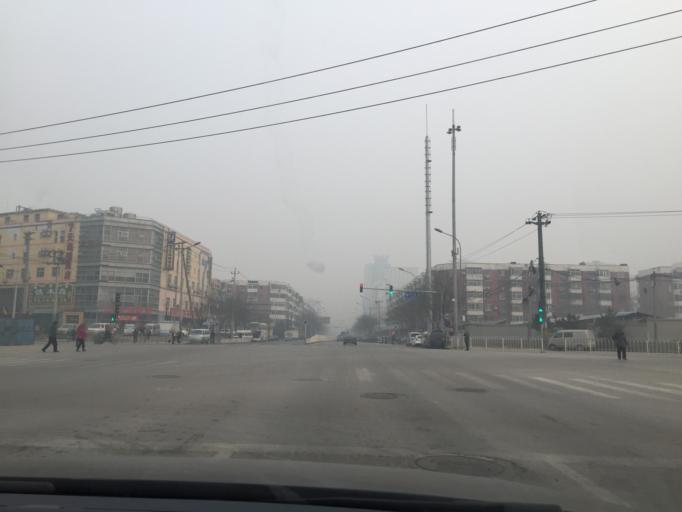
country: CN
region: Beijing
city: Qinghe
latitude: 40.0138
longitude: 116.3387
